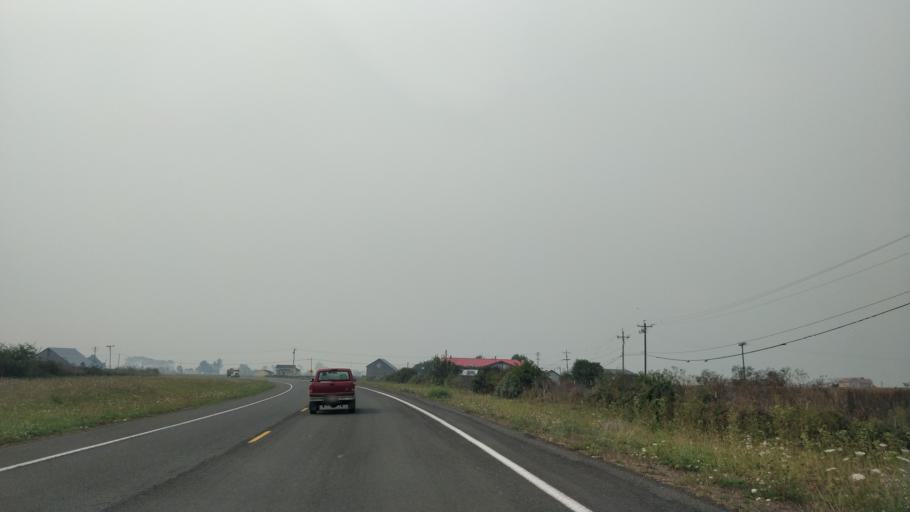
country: US
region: California
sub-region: Humboldt County
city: Ferndale
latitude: 40.5989
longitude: -124.2271
